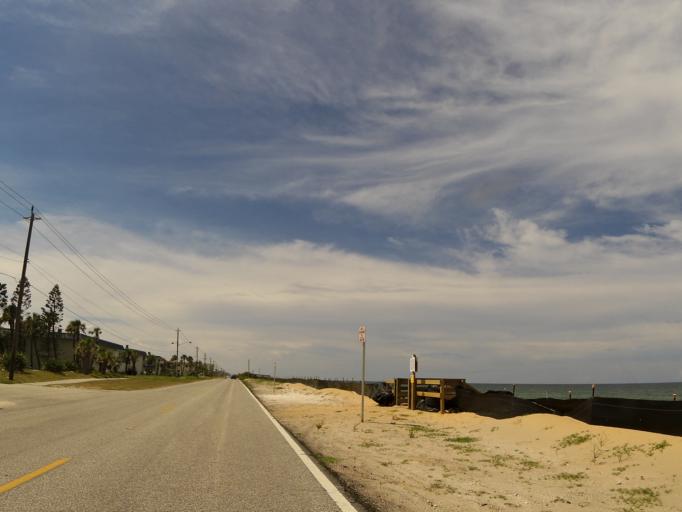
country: US
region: Florida
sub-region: Volusia County
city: Ormond-by-the-Sea
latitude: 29.3590
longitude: -81.0712
